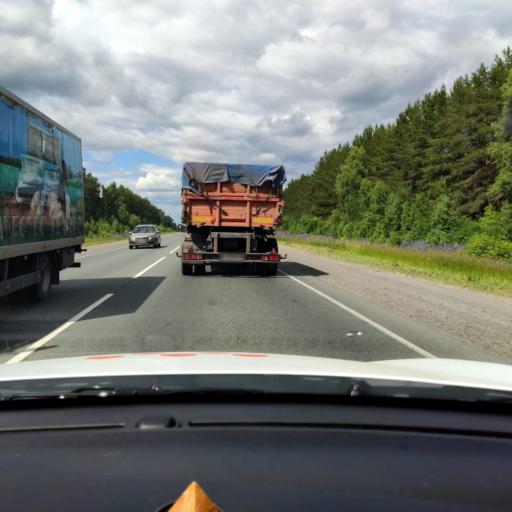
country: RU
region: Mariy-El
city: Pomary
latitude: 55.9475
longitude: 48.3687
